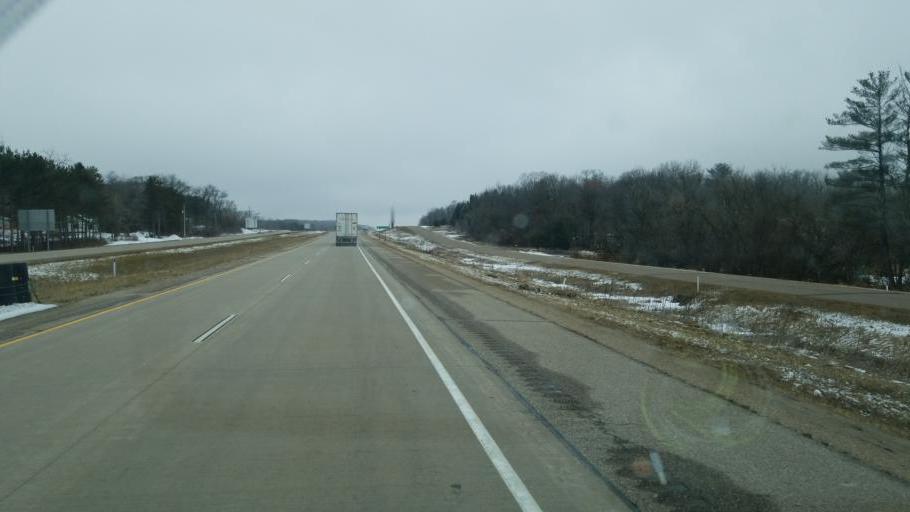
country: US
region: Wisconsin
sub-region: Waupaca County
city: King
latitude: 44.3646
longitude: -89.1324
